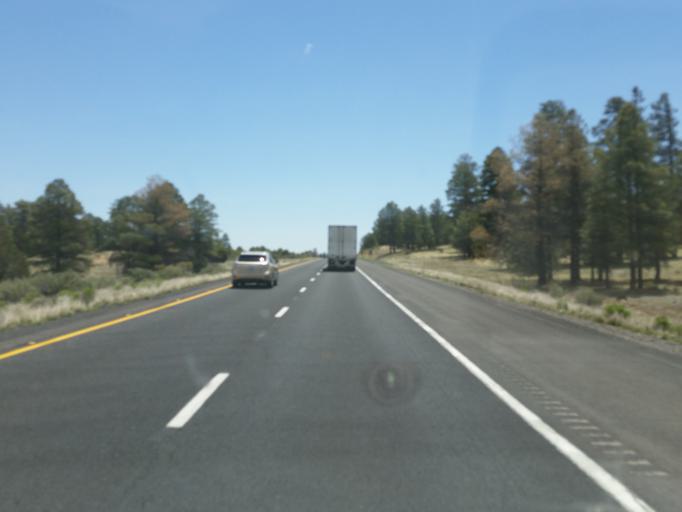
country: US
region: Arizona
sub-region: Coconino County
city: Flagstaff
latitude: 35.2127
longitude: -111.5356
